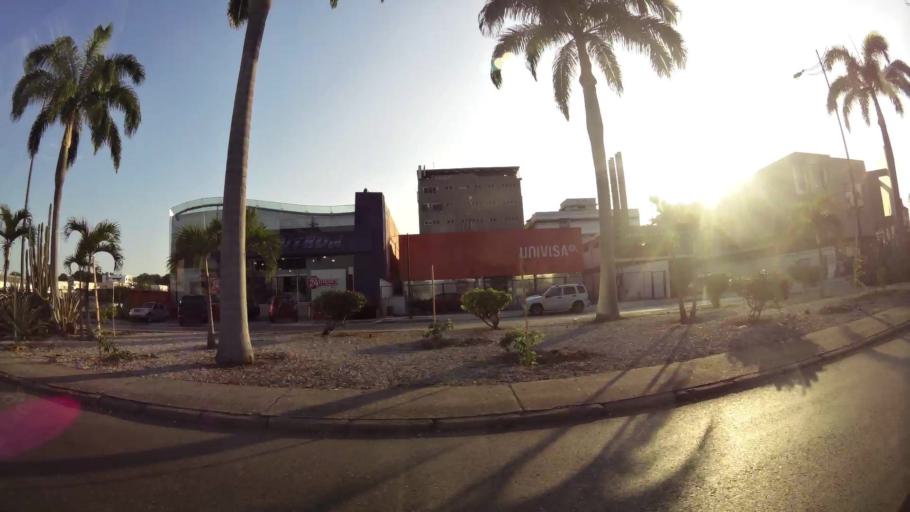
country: EC
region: Guayas
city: Guayaquil
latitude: -2.1608
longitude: -79.8987
